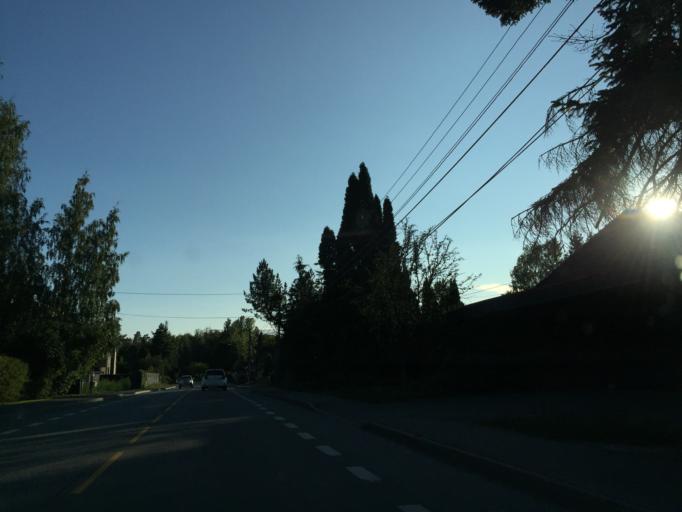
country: NO
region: Akershus
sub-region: Baerum
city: Lysaker
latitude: 59.9052
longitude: 10.5999
